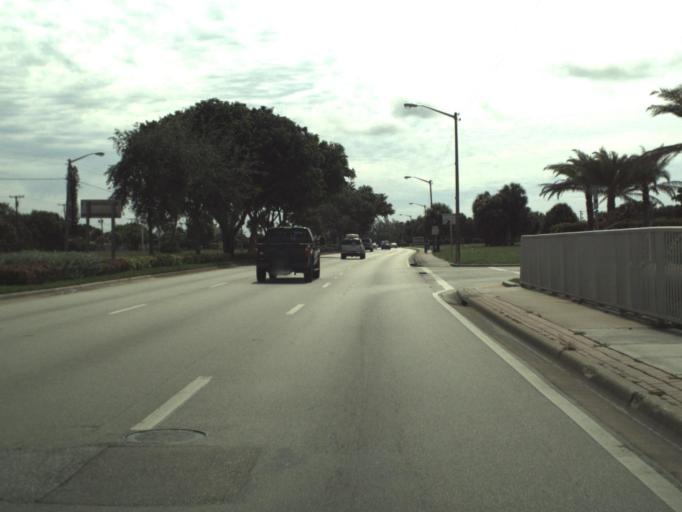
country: US
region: Florida
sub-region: Palm Beach County
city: Mangonia Park
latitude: 26.7810
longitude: -80.0788
